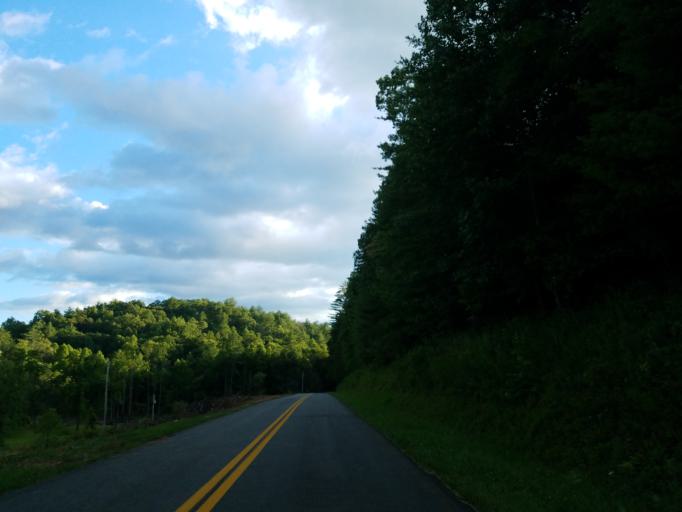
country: US
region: Georgia
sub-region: Union County
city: Blairsville
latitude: 34.7403
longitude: -84.0732
